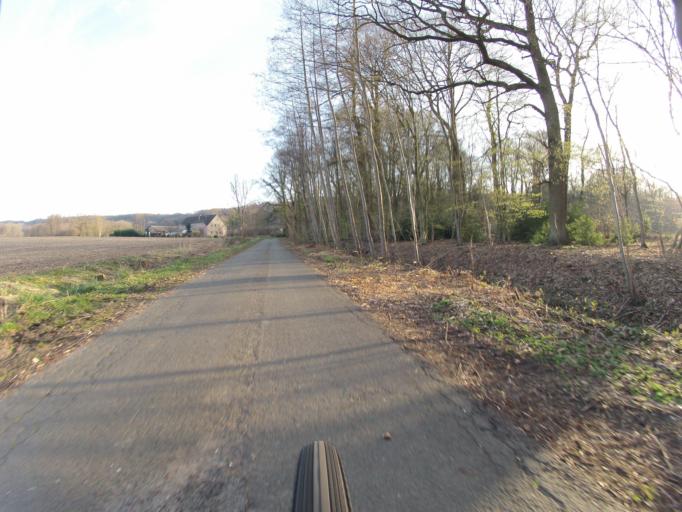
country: DE
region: North Rhine-Westphalia
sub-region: Regierungsbezirk Munster
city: Tecklenburg
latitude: 52.2387
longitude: 7.7627
